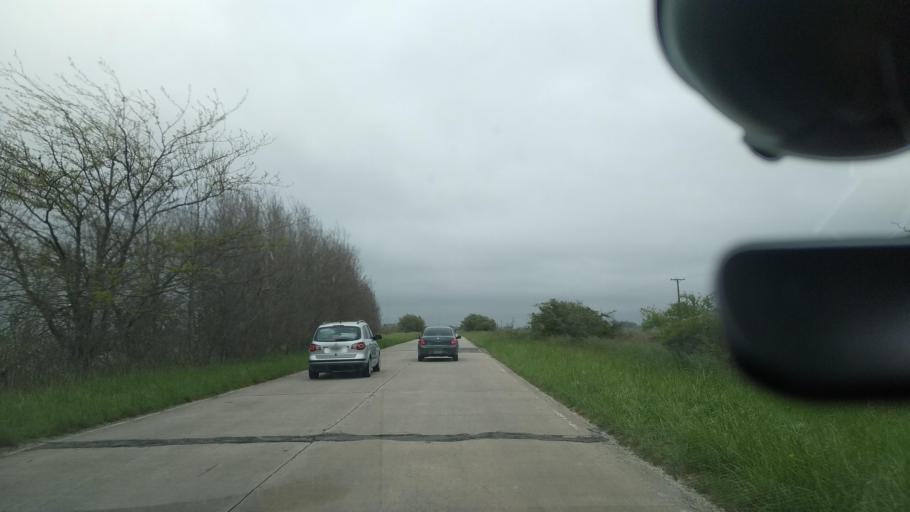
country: AR
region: Buenos Aires
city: Veronica
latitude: -35.5565
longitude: -57.3052
